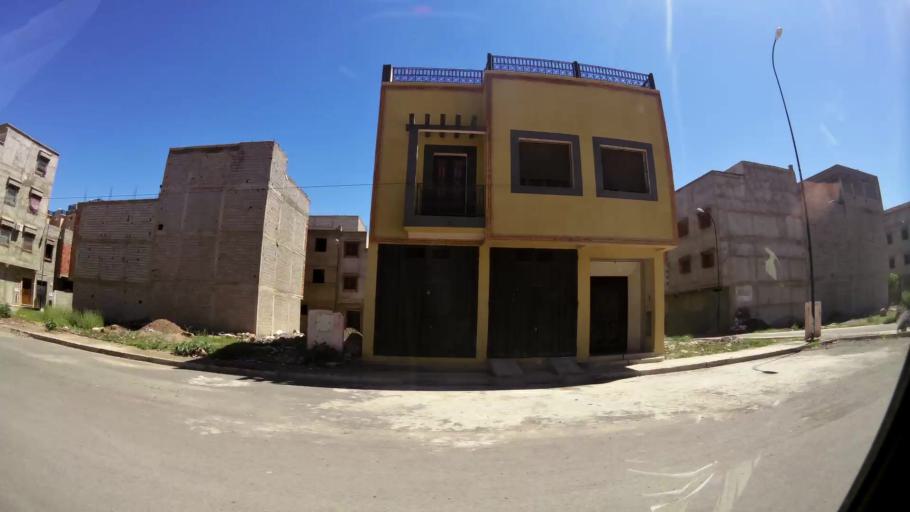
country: MA
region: Marrakech-Tensift-Al Haouz
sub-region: Marrakech
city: Marrakesh
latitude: 31.5541
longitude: -7.9794
